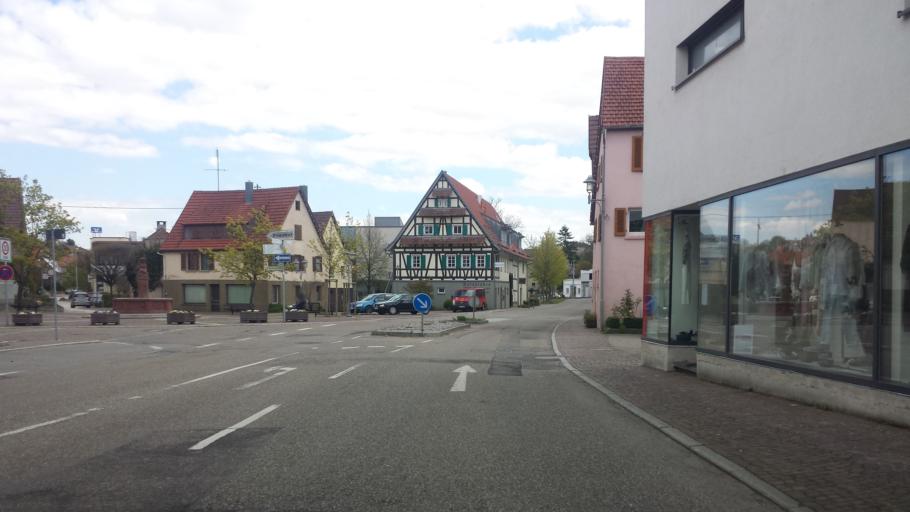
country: DE
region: Baden-Wuerttemberg
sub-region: Regierungsbezirk Stuttgart
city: Weissach
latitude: 48.8467
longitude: 8.9270
